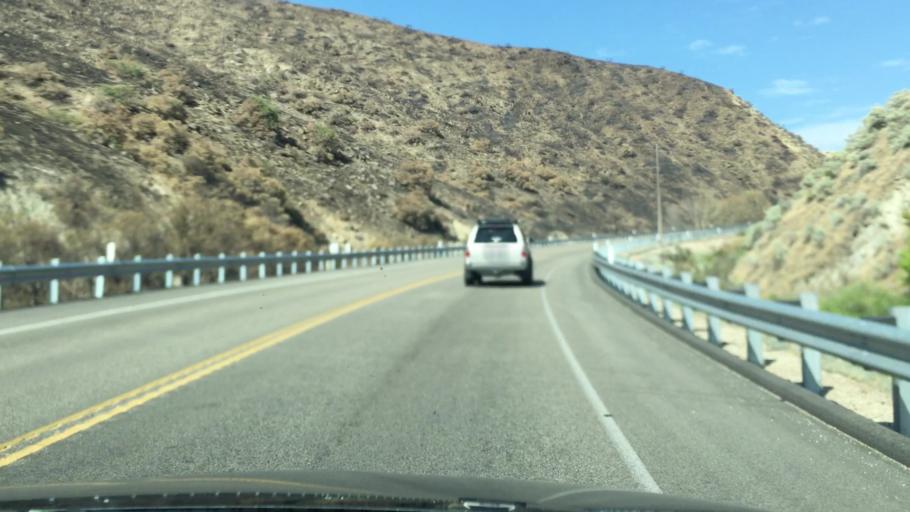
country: US
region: Idaho
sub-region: Ada County
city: Eagle
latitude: 43.7598
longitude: -116.2734
